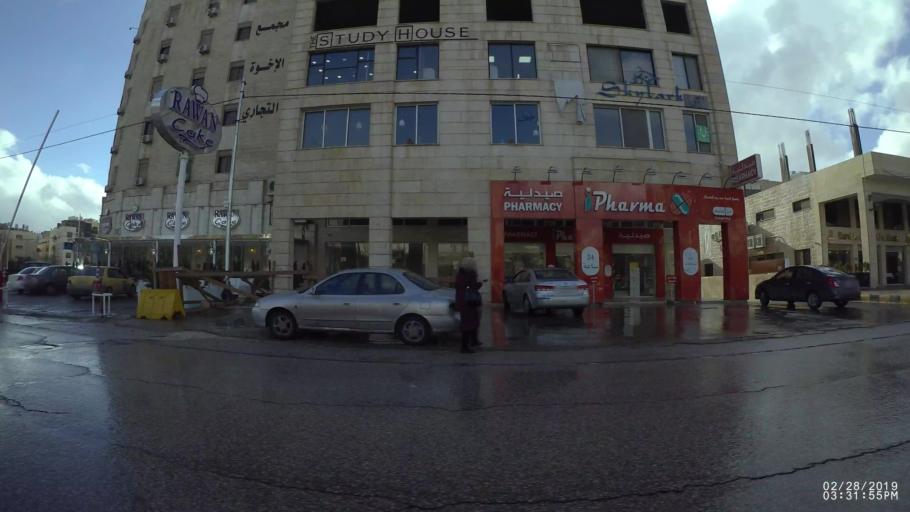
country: JO
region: Amman
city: Al Jubayhah
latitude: 32.0068
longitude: 35.8723
